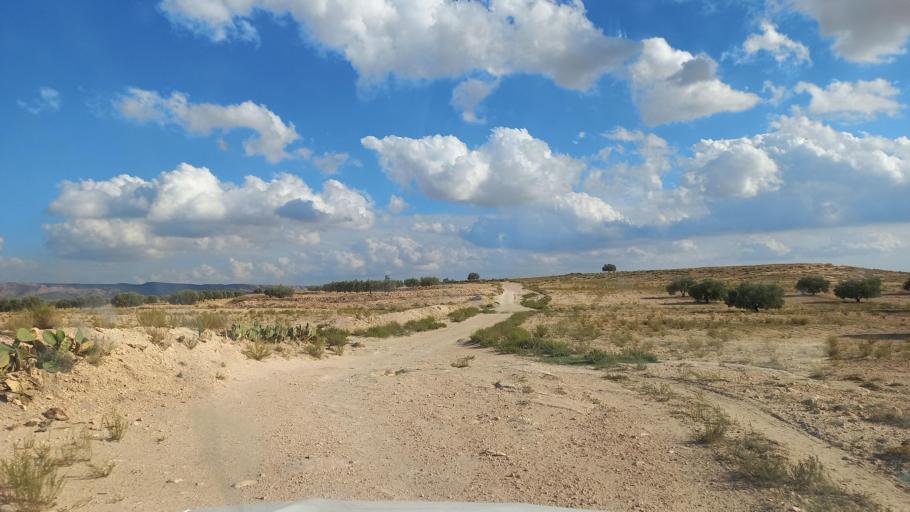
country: TN
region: Al Qasrayn
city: Sbiba
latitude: 35.3958
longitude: 9.0395
